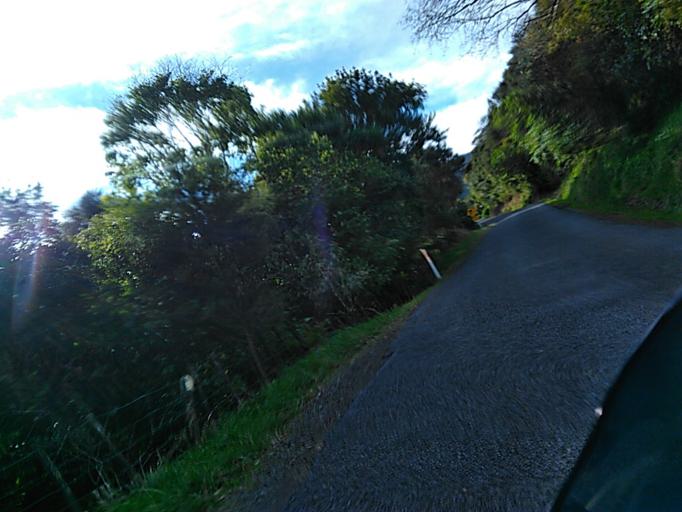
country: NZ
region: Gisborne
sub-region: Gisborne District
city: Gisborne
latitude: -38.6273
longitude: 178.0526
